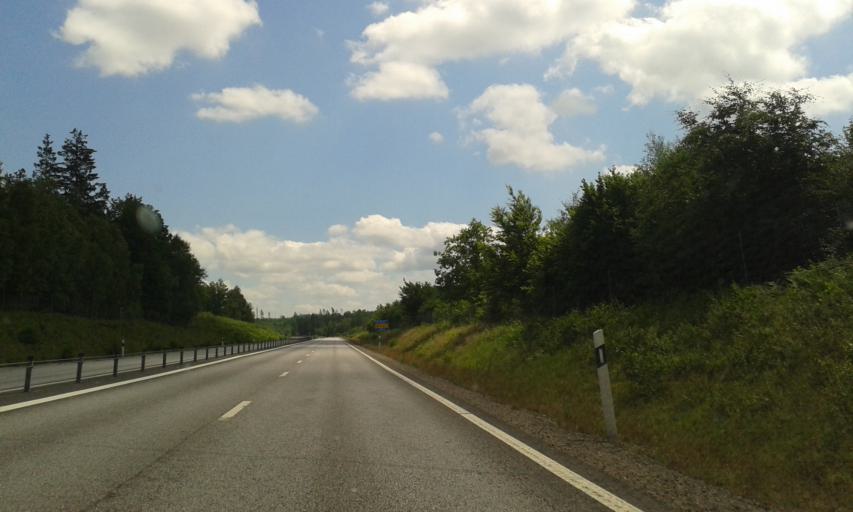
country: SE
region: Kronoberg
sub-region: Vaxjo Kommun
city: Gemla
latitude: 56.9001
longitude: 14.6749
